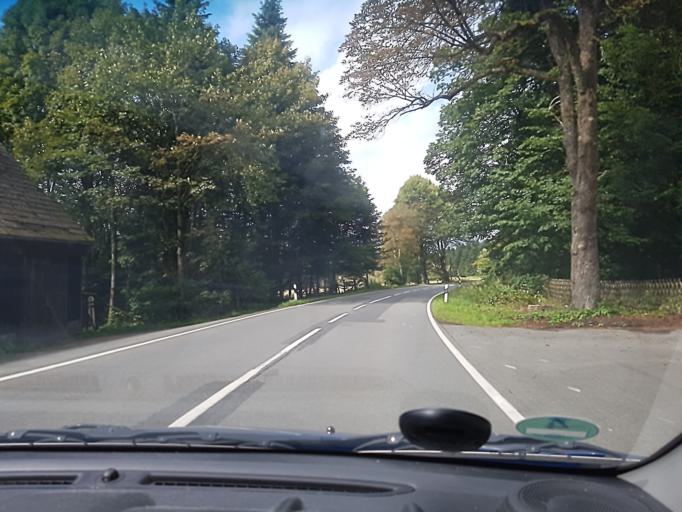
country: DE
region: Lower Saxony
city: Heinade
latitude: 51.7637
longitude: 9.5623
